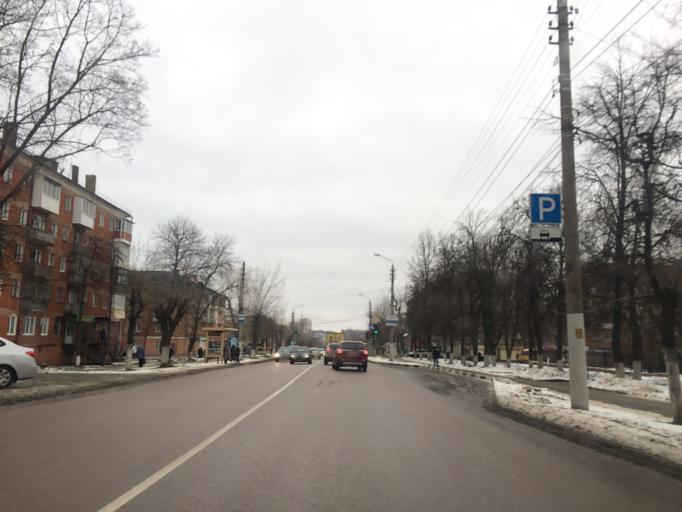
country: RU
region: Tula
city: Tula
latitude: 54.2103
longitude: 37.6694
